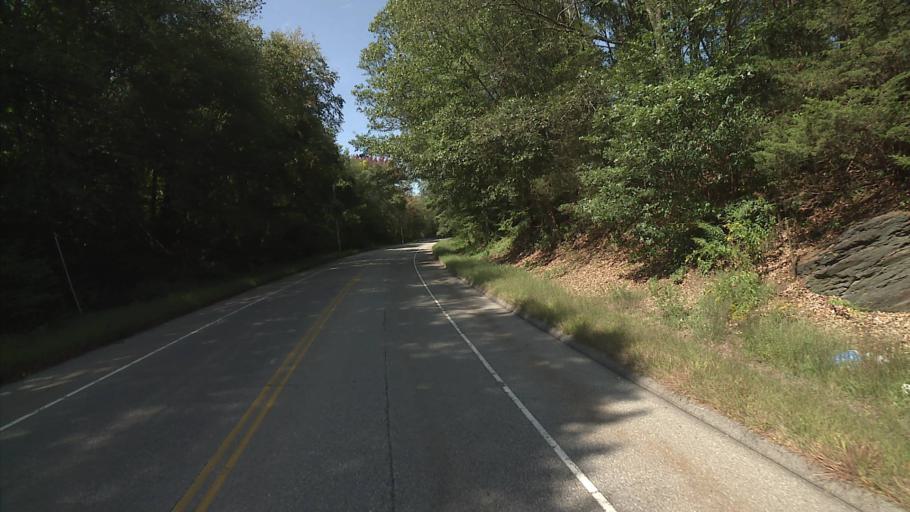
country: US
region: Connecticut
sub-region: New London County
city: Baltic
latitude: 41.5844
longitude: -72.1540
